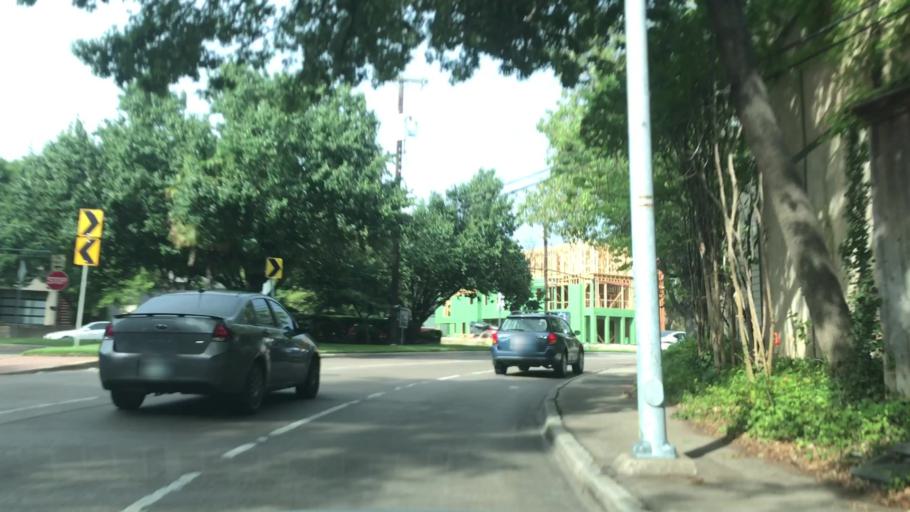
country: US
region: Texas
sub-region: Dallas County
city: Highland Park
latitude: 32.8182
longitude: -96.7975
